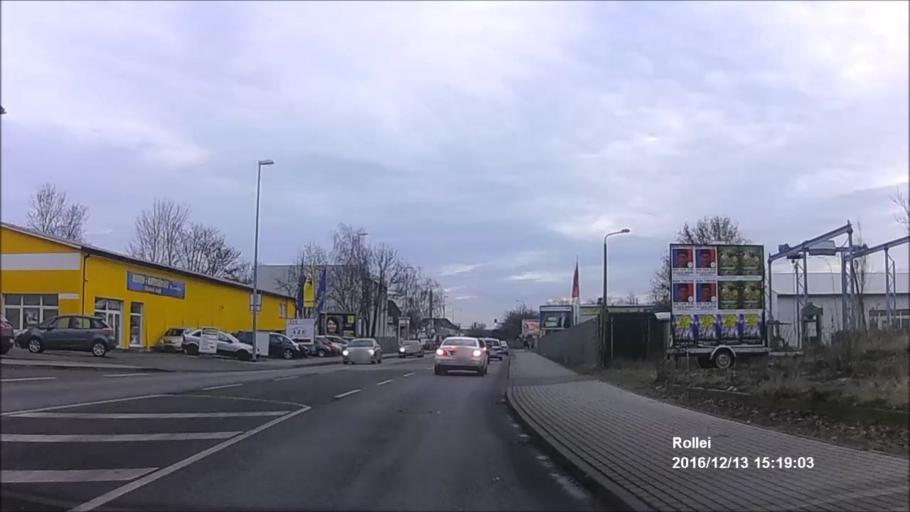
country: DE
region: Thuringia
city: Erfurt
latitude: 51.0093
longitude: 11.0177
